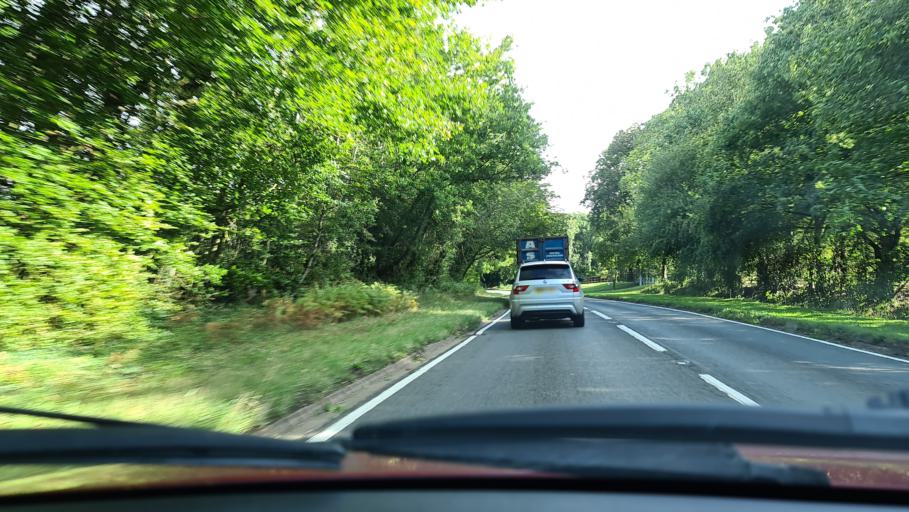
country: GB
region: England
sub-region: Buckinghamshire
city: Amersham
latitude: 51.6457
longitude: -0.6188
